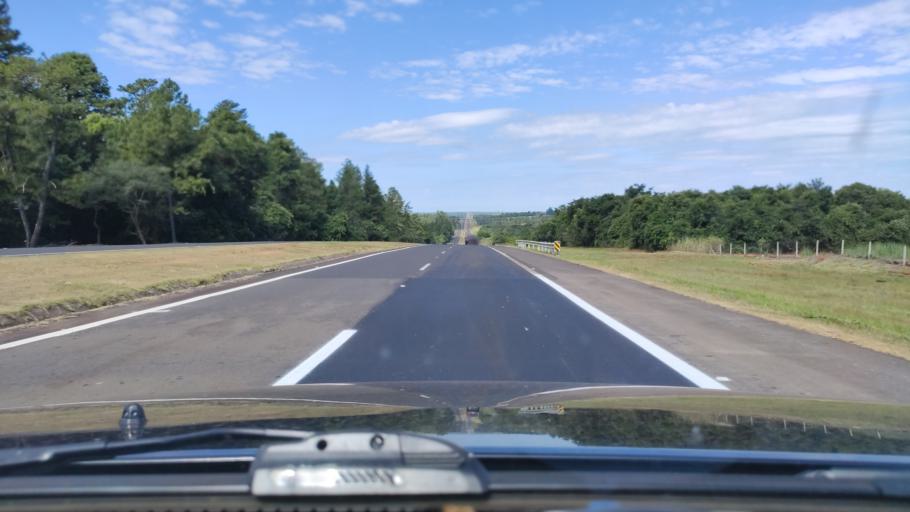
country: BR
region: Sao Paulo
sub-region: Rancharia
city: Rancharia
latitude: -22.4671
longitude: -50.9525
